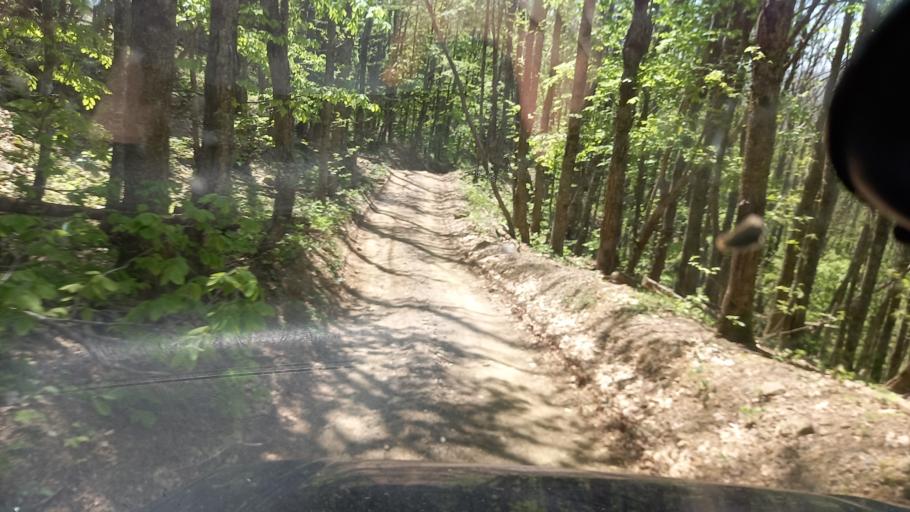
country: RU
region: Krasnodarskiy
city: Tuapse
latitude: 44.2508
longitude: 39.2857
